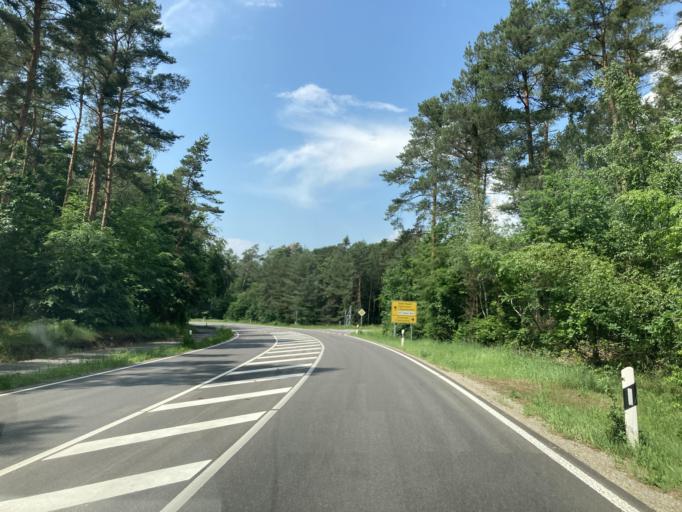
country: DE
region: Baden-Wuerttemberg
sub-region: Karlsruhe Region
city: Eggenstein-Leopoldshafen
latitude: 49.0902
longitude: 8.4479
